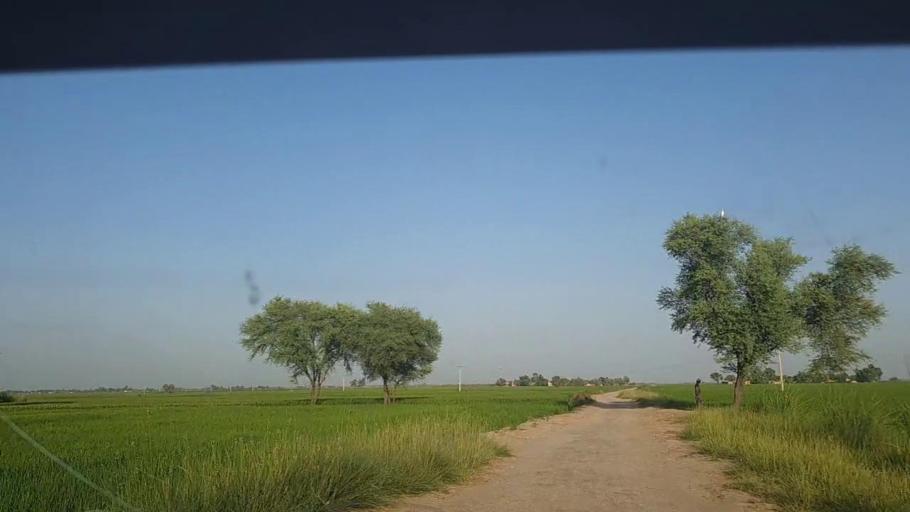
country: PK
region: Sindh
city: Thul
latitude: 28.2134
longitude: 68.8785
